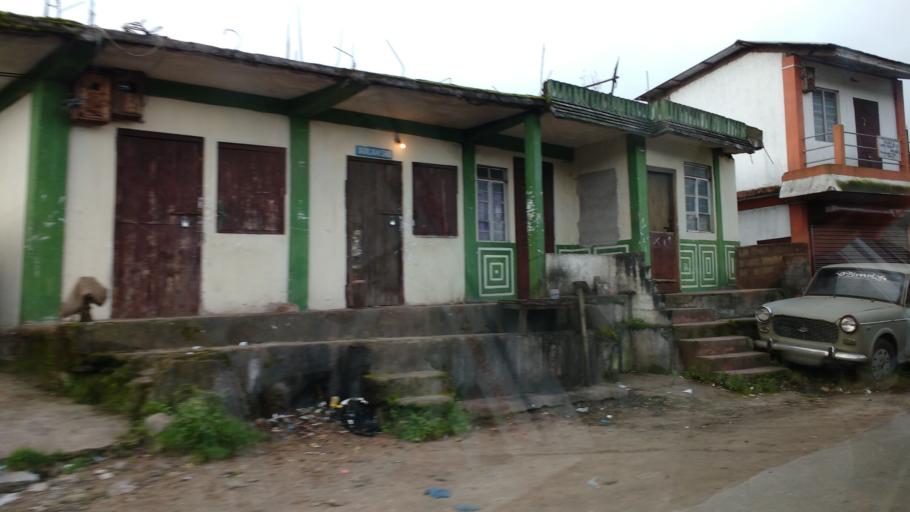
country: IN
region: Meghalaya
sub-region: East Khasi Hills
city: Shillong
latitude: 25.5296
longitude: 91.8216
